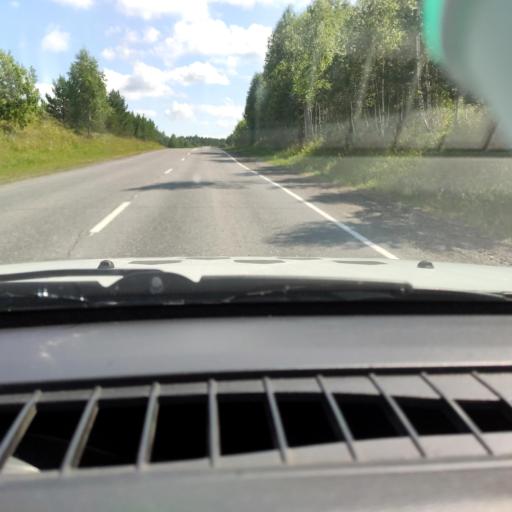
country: RU
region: Chelyabinsk
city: Mezhevoy
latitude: 55.2925
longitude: 58.7638
